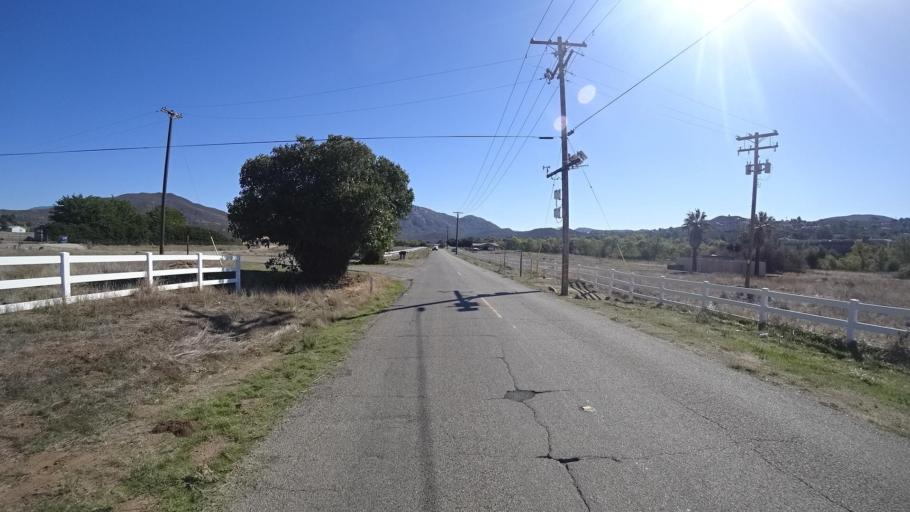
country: US
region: California
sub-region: San Diego County
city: Alpine
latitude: 32.8456
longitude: -116.7063
